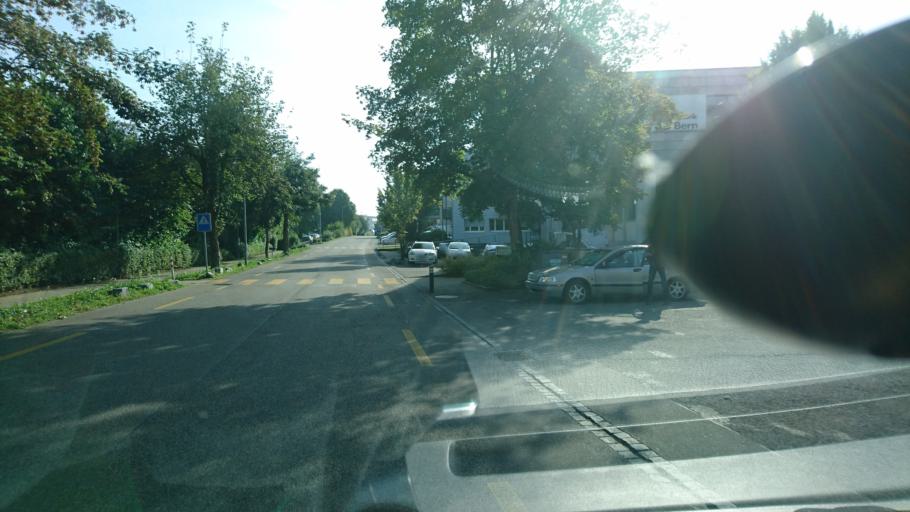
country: CH
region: Bern
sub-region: Bern-Mittelland District
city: Zollikofen
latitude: 47.0019
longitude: 7.4434
